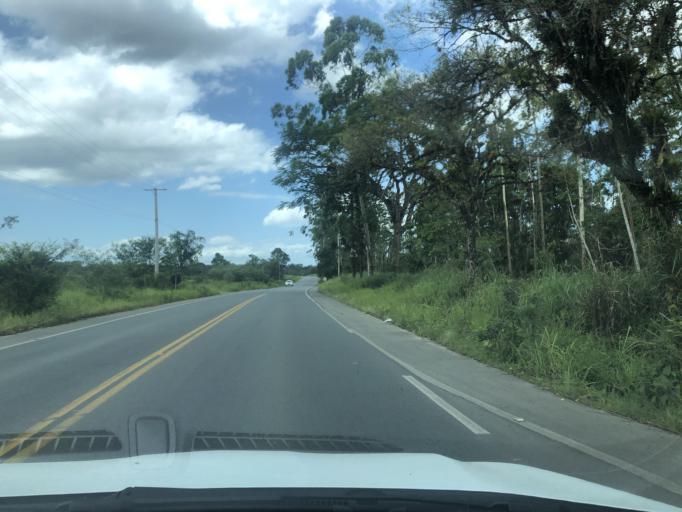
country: BR
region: Santa Catarina
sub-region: Joinville
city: Joinville
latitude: -26.4072
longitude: -48.7588
